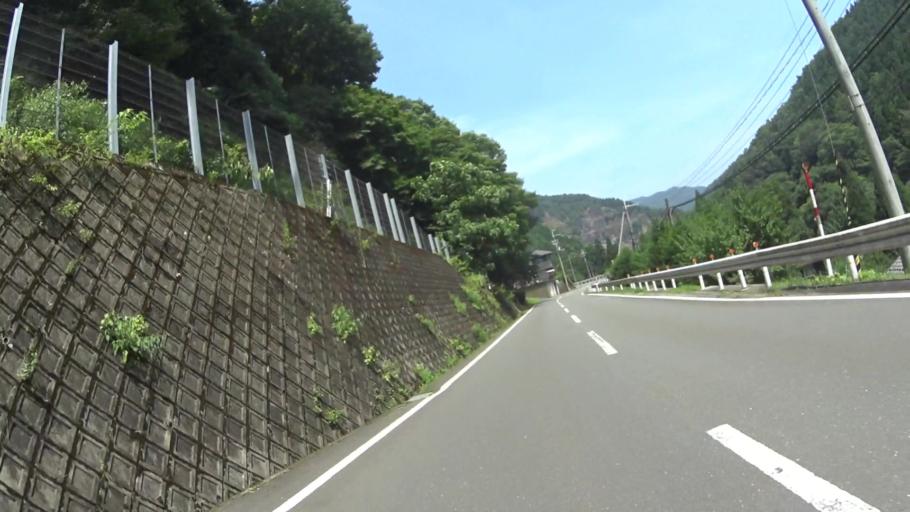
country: JP
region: Kyoto
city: Ayabe
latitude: 35.2865
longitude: 135.4273
